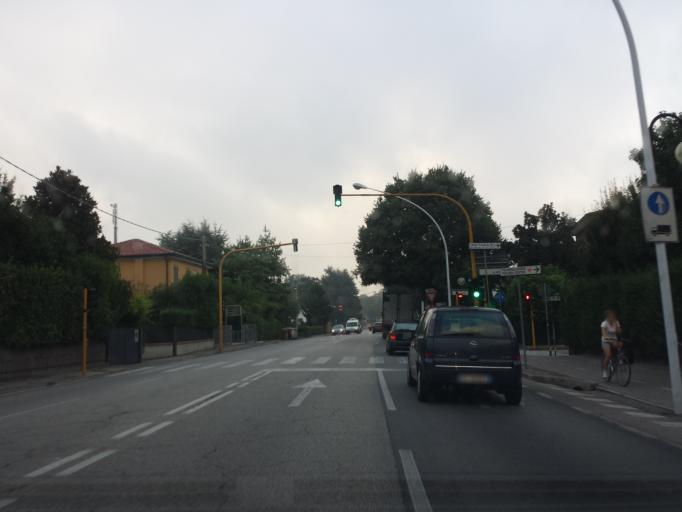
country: IT
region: Veneto
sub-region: Provincia di Padova
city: Caselle
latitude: 45.4112
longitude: 11.8461
